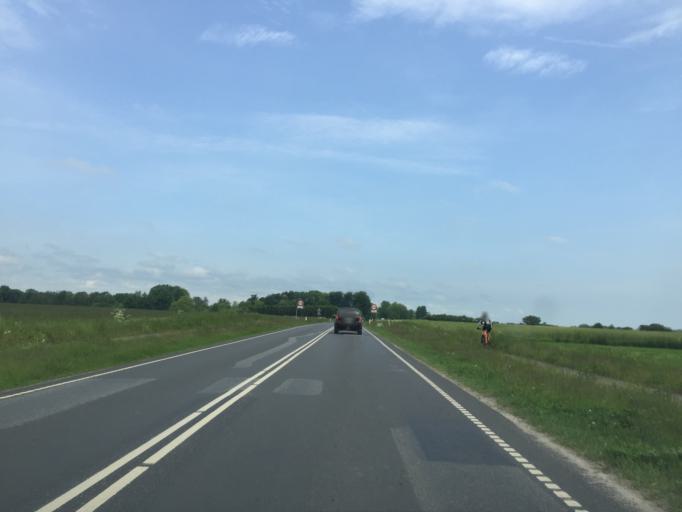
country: DK
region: South Denmark
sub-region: Svendborg Kommune
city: Thuro By
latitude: 55.1320
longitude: 10.7327
